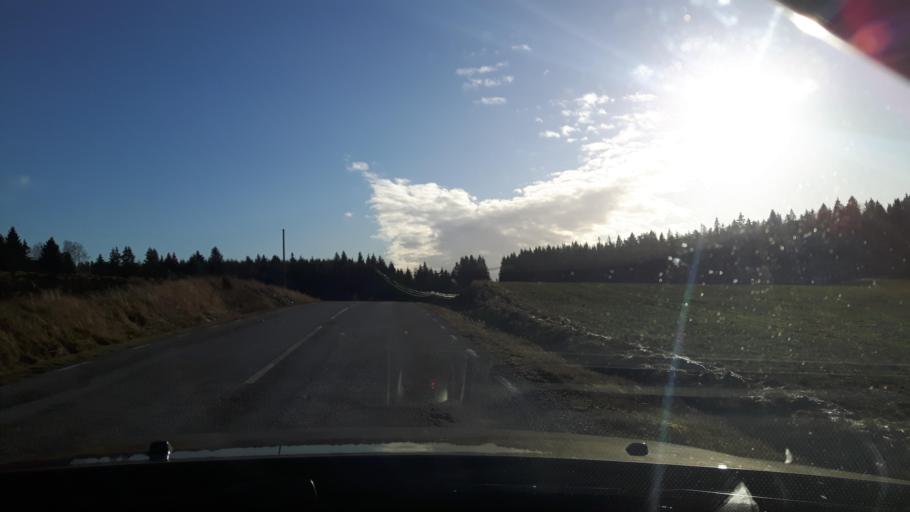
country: SE
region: Vaestra Goetaland
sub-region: Munkedals Kommun
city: Munkedal
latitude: 58.5762
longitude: 11.7327
